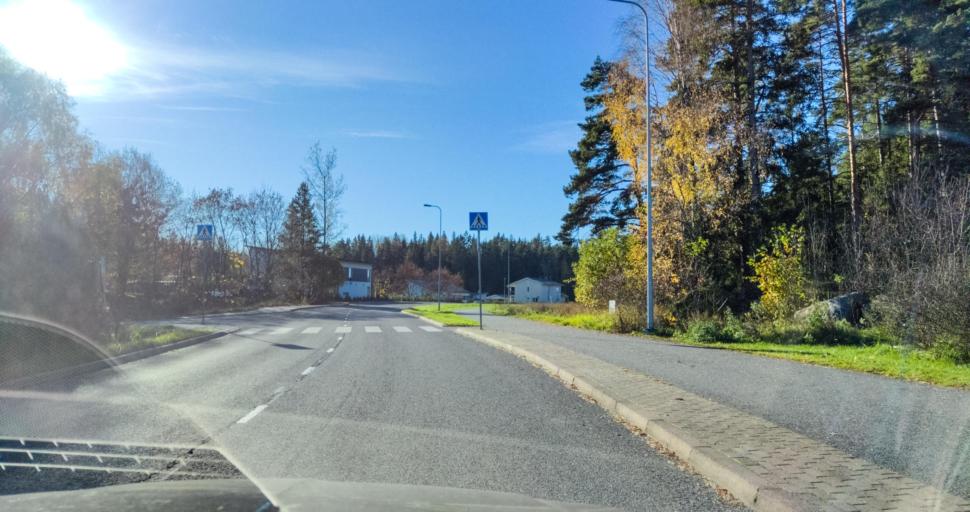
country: FI
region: Varsinais-Suomi
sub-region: Turku
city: Turku
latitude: 60.4067
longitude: 22.2170
